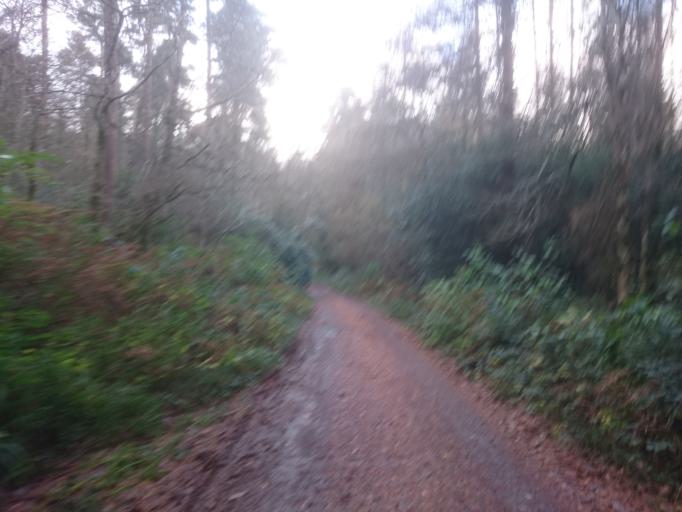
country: IE
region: Leinster
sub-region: Kilkenny
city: Thomastown
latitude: 52.4709
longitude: -7.0617
